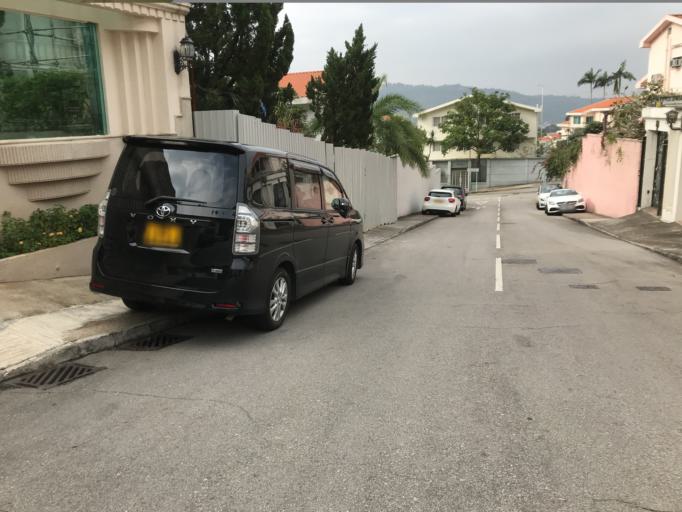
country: HK
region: Tai Po
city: Tai Po
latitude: 22.4615
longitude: 114.1588
